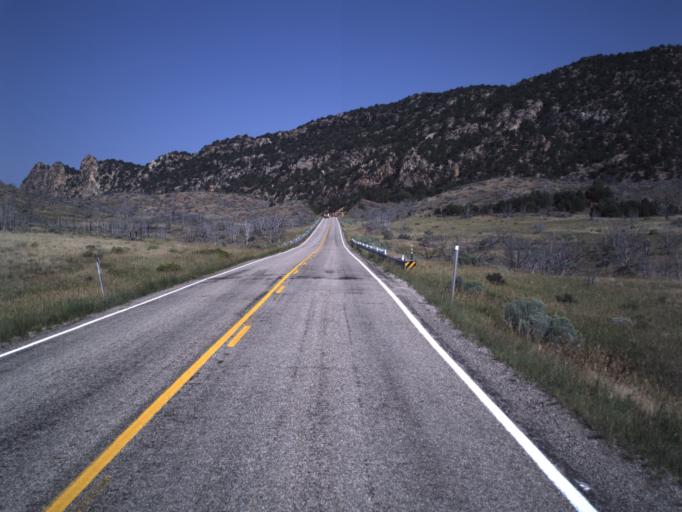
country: US
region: Utah
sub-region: Daggett County
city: Manila
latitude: 40.9499
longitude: -109.4450
